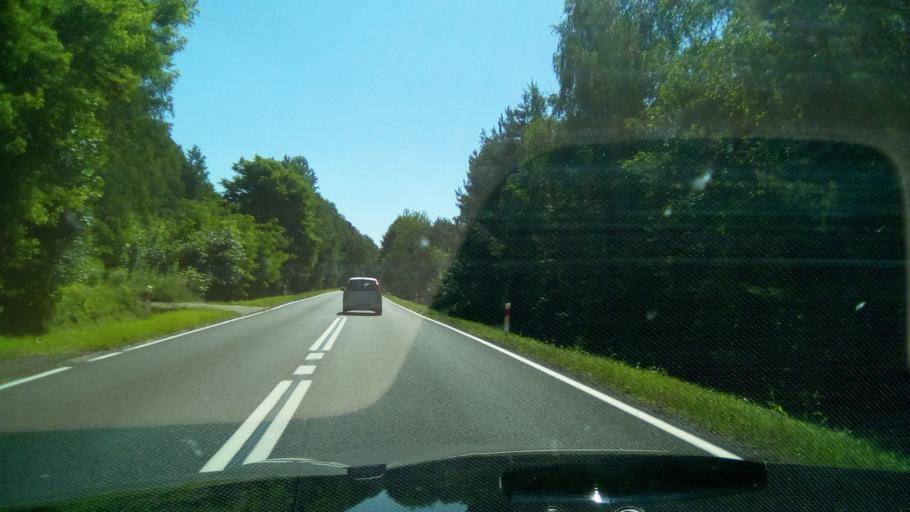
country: PL
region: Lodz Voivodeship
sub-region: Powiat tomaszowski
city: Inowlodz
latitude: 51.5263
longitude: 20.1882
